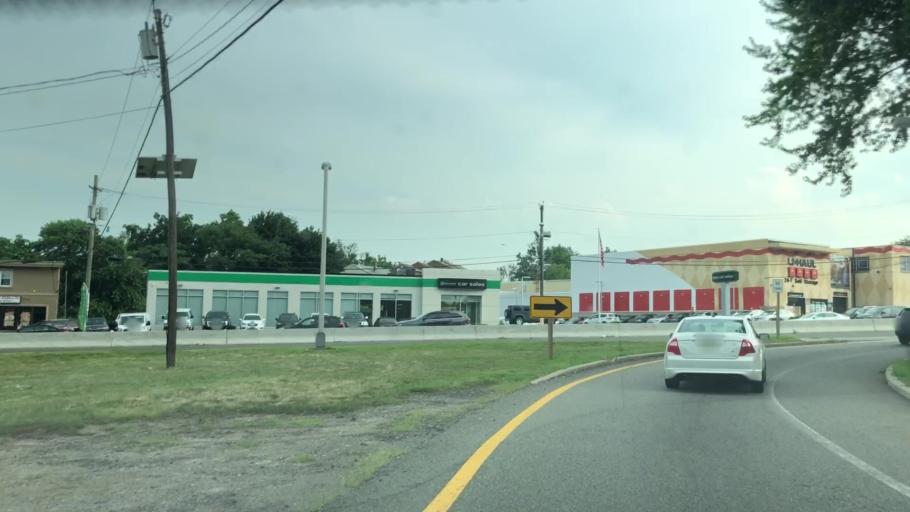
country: US
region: New Jersey
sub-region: Bergen County
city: Elmwood Park
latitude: 40.8937
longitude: -74.1215
